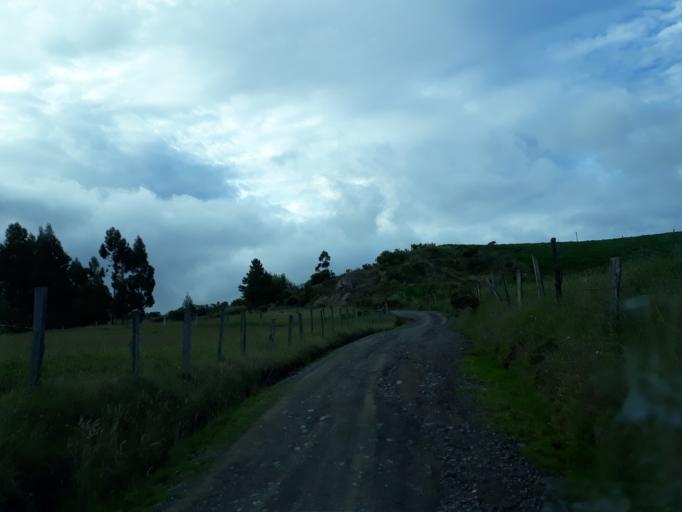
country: CO
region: Cundinamarca
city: Carmen de Carupa
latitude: 5.3132
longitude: -73.9100
